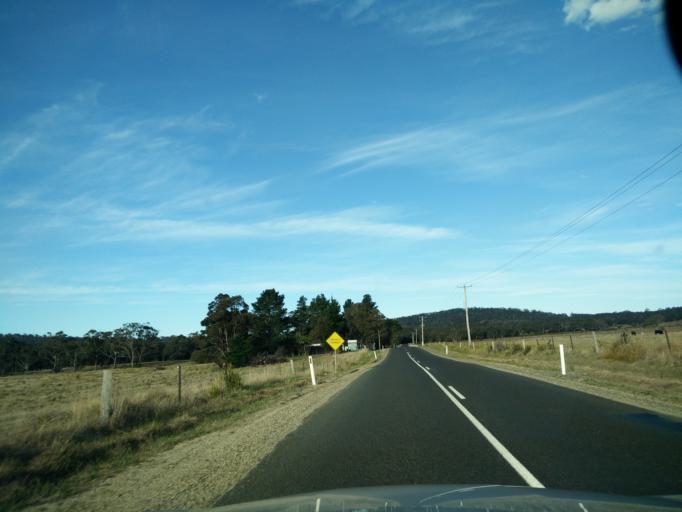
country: AU
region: Tasmania
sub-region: Break O'Day
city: St Helens
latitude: -41.8920
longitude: 148.2656
